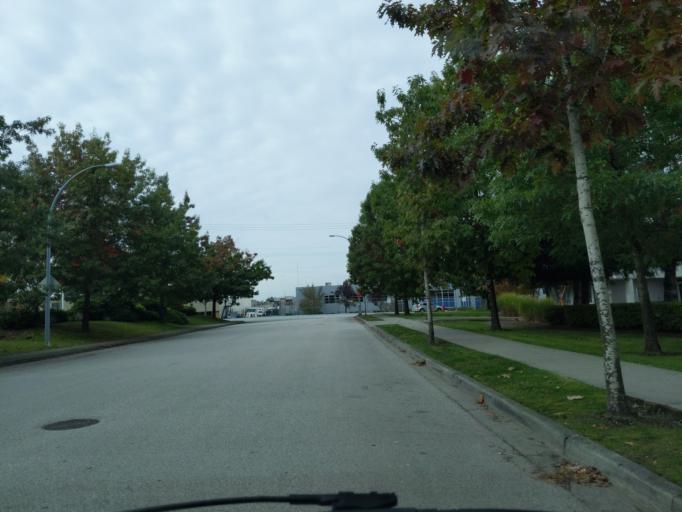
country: CA
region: British Columbia
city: Walnut Grove
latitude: 49.1793
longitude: -122.6633
